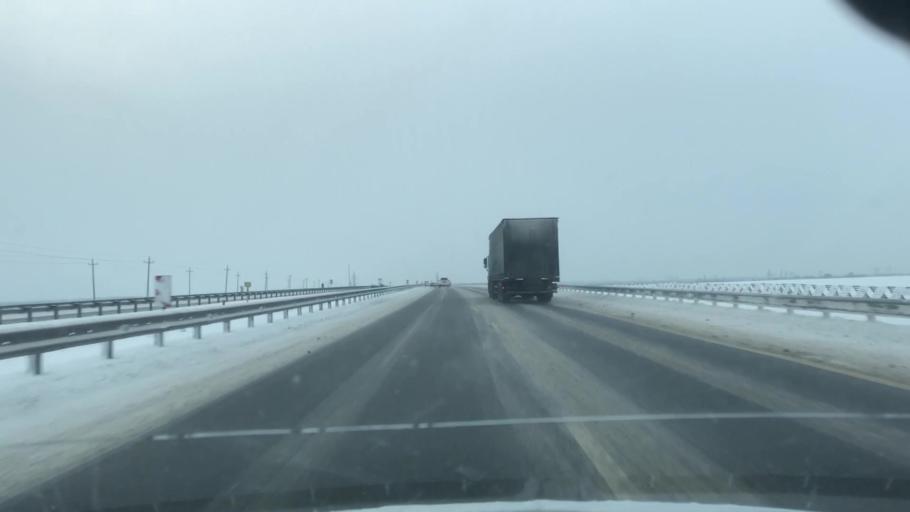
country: RU
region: Moskovskaya
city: Mikhnevo
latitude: 55.1076
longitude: 37.9261
